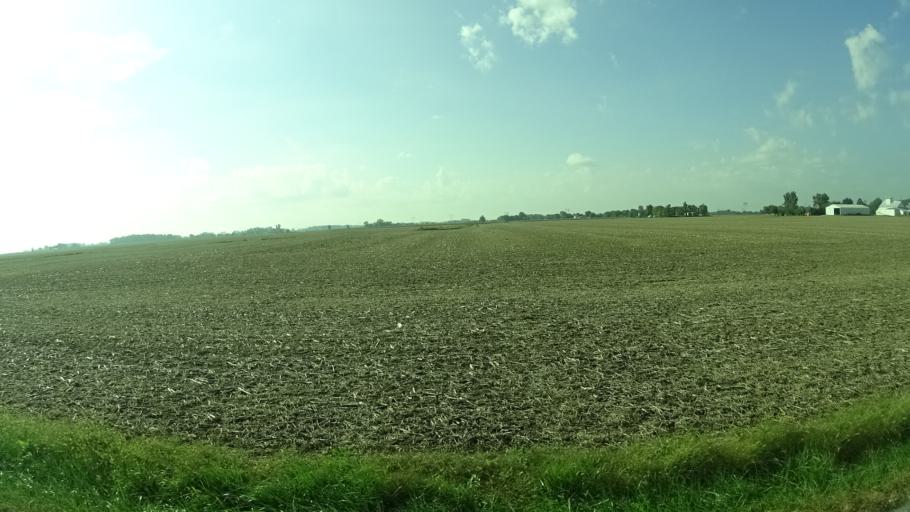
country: US
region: Indiana
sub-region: Madison County
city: Lapel
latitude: 40.0455
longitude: -85.8394
